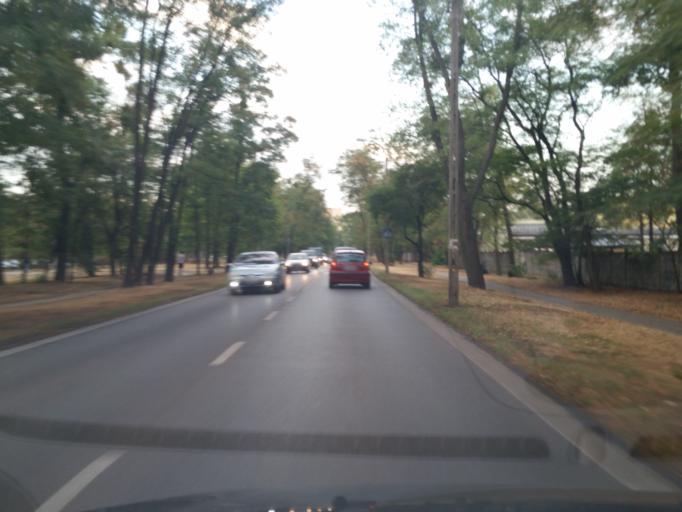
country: PL
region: Masovian Voivodeship
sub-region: Warszawa
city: Bemowo
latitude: 52.2574
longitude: 20.9011
